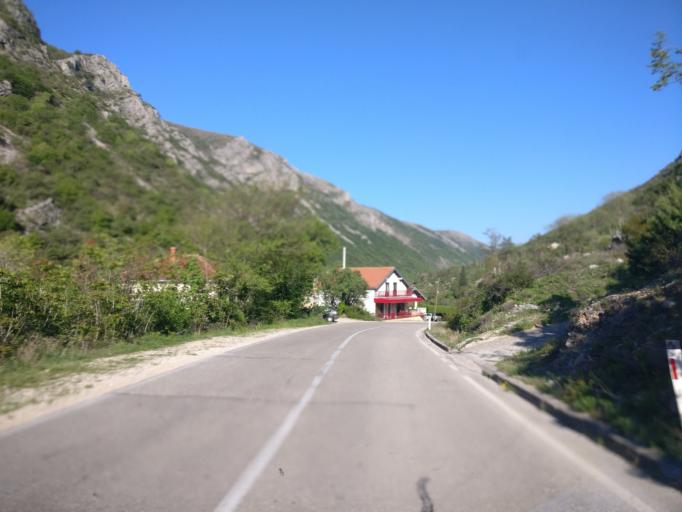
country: BA
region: Federation of Bosnia and Herzegovina
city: Stolac
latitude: 43.0768
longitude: 18.0238
